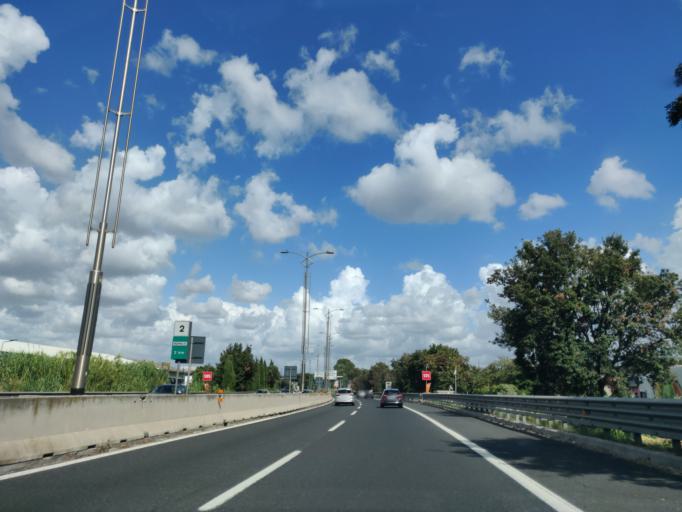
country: IT
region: Latium
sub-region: Citta metropolitana di Roma Capitale
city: Vitinia
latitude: 41.8313
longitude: 12.4365
